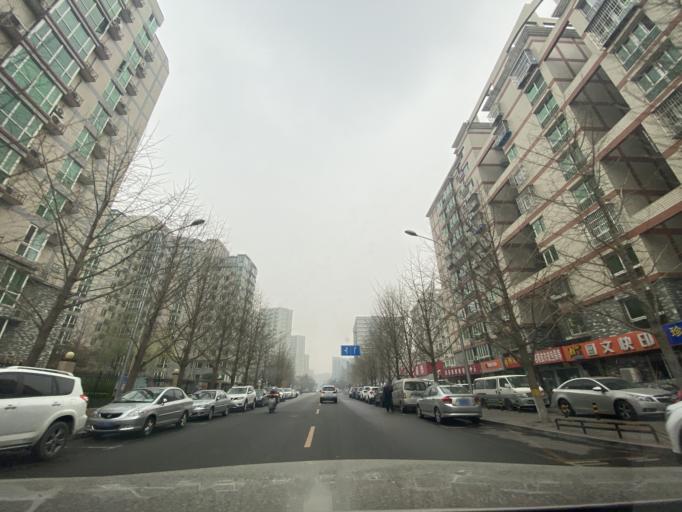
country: CN
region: Beijing
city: Sijiqing
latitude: 39.9616
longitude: 116.2740
